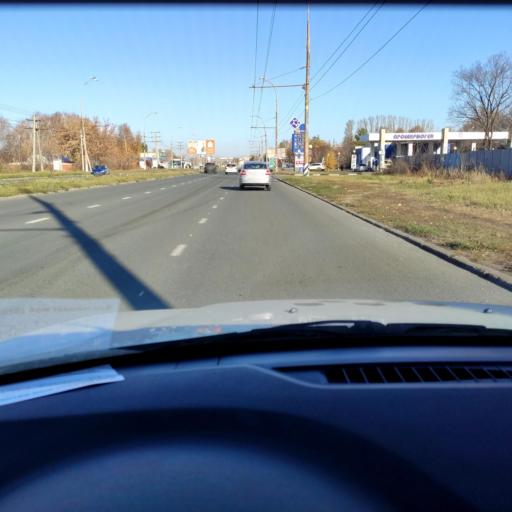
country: RU
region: Samara
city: Tol'yatti
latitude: 53.5469
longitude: 49.3019
